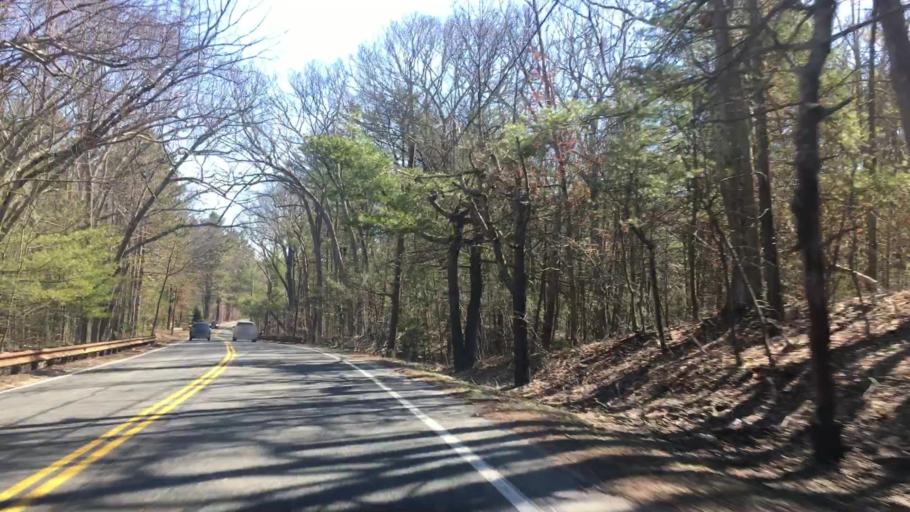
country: US
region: Massachusetts
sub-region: Middlesex County
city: Sherborn
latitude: 42.2532
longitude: -71.3563
